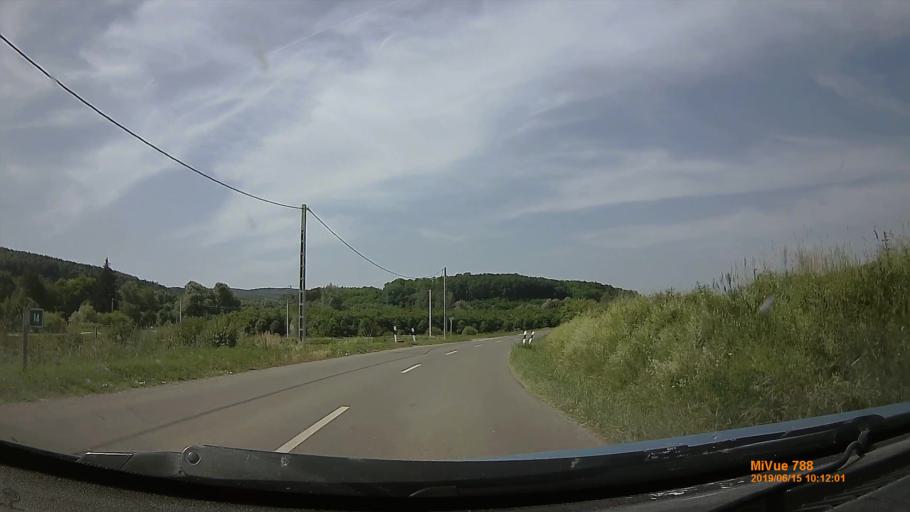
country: HU
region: Baranya
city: Buekkoesd
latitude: 46.1405
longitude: 18.0585
